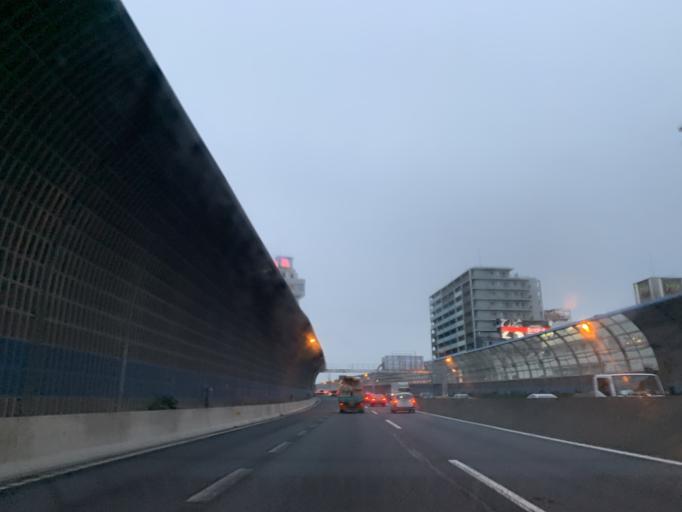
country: JP
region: Chiba
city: Funabashi
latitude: 35.6877
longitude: 139.9982
